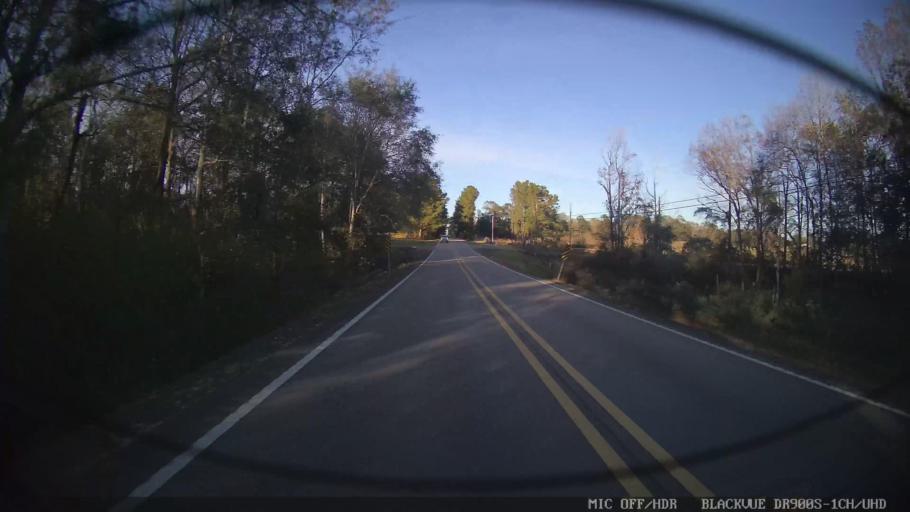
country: US
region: Mississippi
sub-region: Lamar County
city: Lumberton
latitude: 31.0486
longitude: -89.4335
